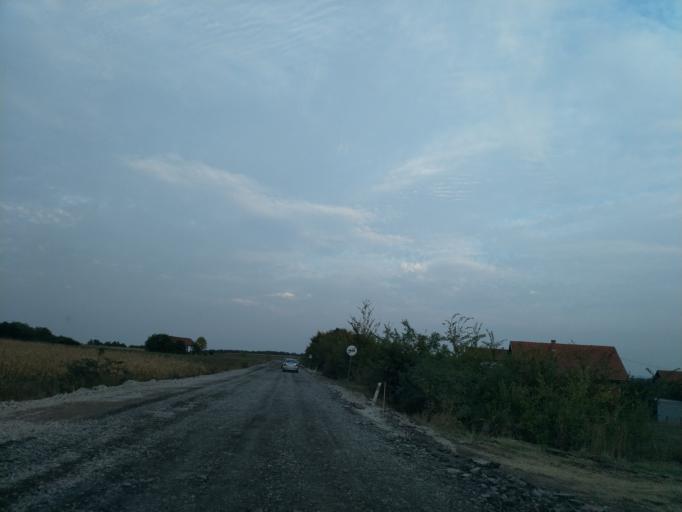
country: RS
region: Central Serbia
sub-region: Sumadijski Okrug
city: Kragujevac
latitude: 44.1045
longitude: 20.8469
